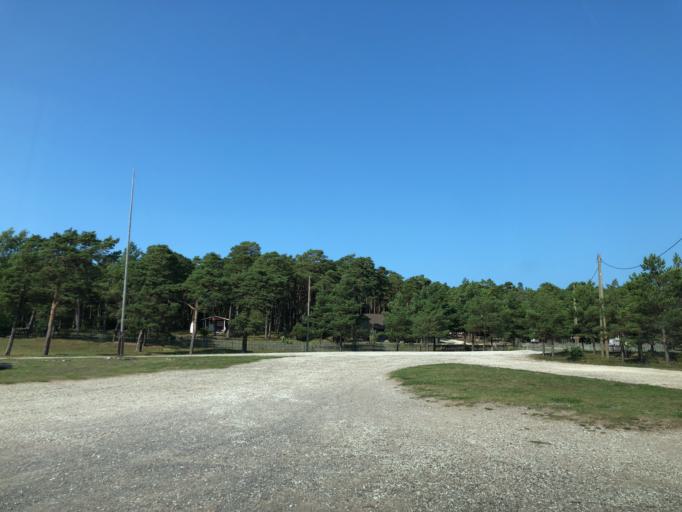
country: EE
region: Hiiumaa
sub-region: Kaerdla linn
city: Kardla
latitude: 58.9212
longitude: 22.0563
